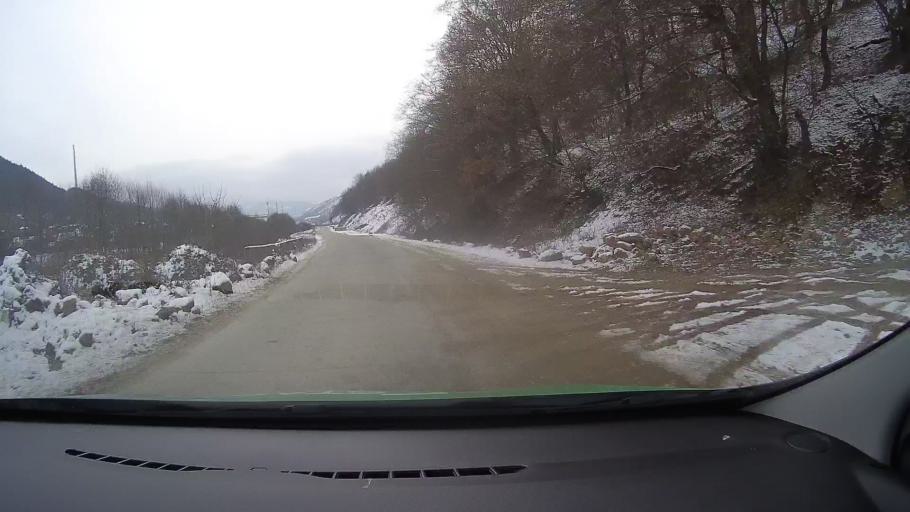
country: RO
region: Alba
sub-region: Oras Zlatna
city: Zlatna
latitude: 46.1173
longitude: 23.2062
